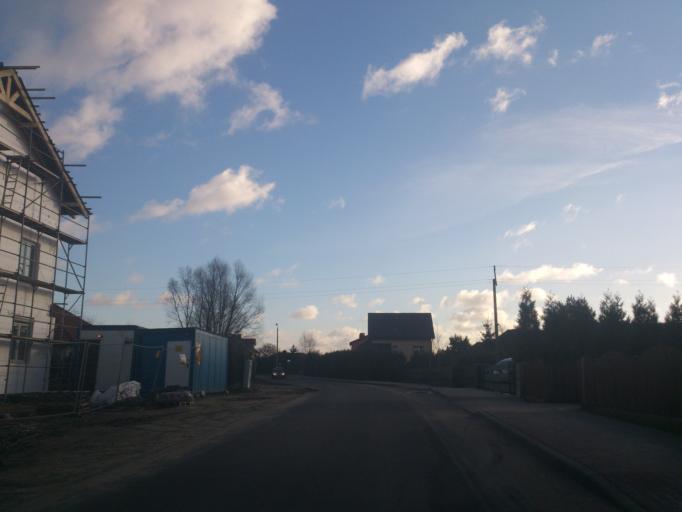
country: PL
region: Kujawsko-Pomorskie
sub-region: Powiat torunski
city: Lubicz Gorny
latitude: 53.0237
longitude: 18.8046
